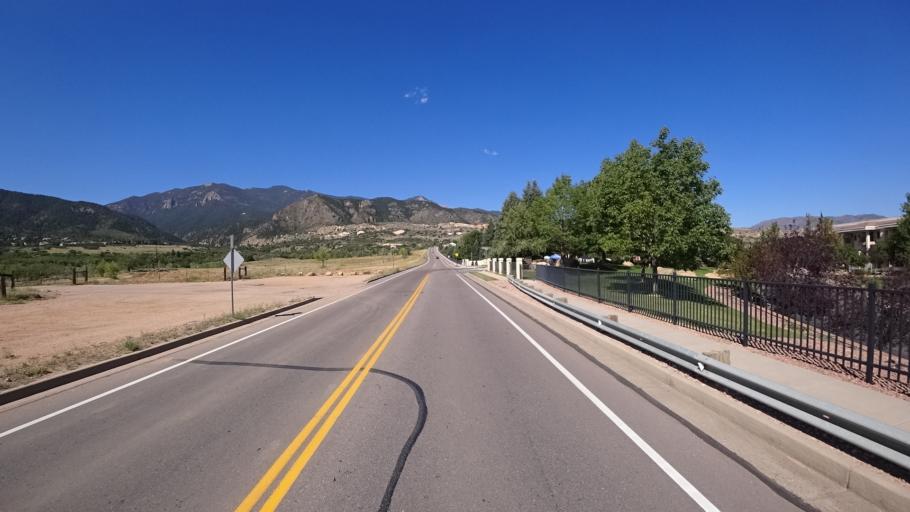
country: US
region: Colorado
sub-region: El Paso County
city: Colorado Springs
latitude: 38.8304
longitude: -104.8712
